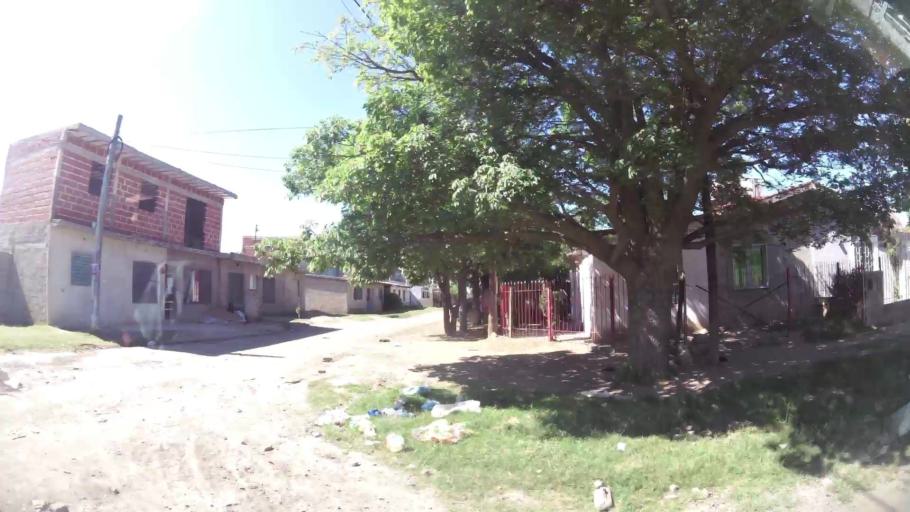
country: AR
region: Cordoba
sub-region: Departamento de Capital
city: Cordoba
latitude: -31.4448
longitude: -64.1320
